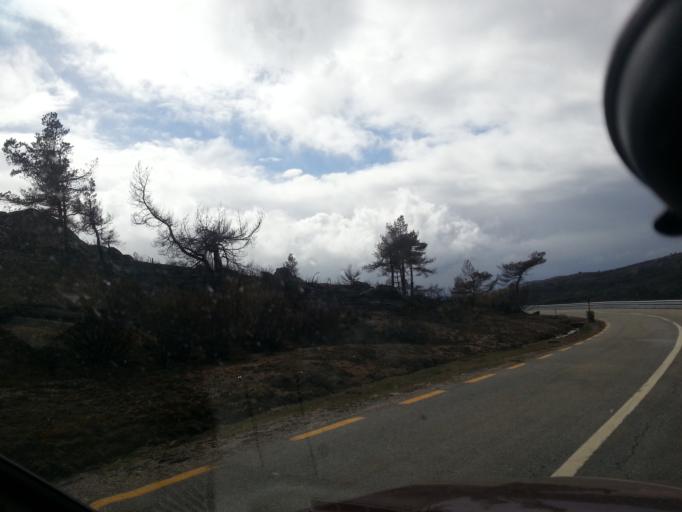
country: PT
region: Guarda
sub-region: Manteigas
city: Manteigas
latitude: 40.4230
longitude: -7.5925
